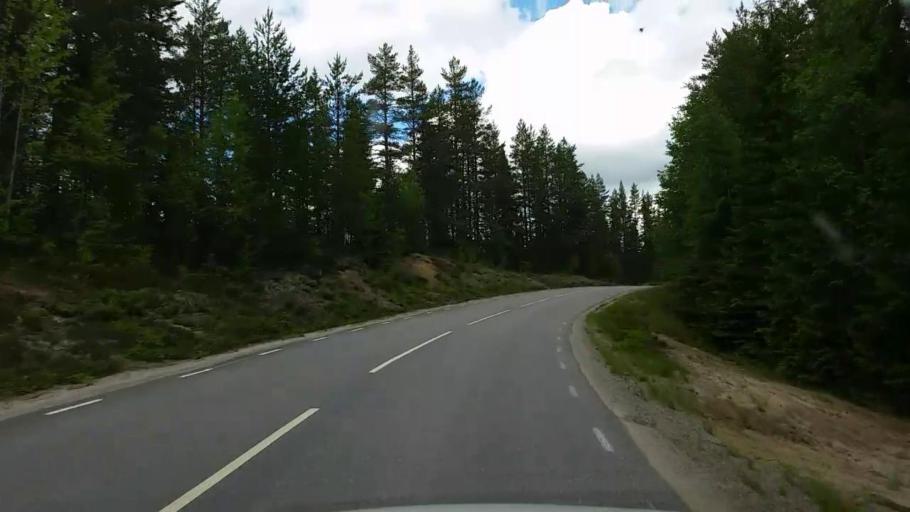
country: SE
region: Gaevleborg
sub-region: Bollnas Kommun
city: Vittsjo
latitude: 61.1148
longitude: 16.1471
